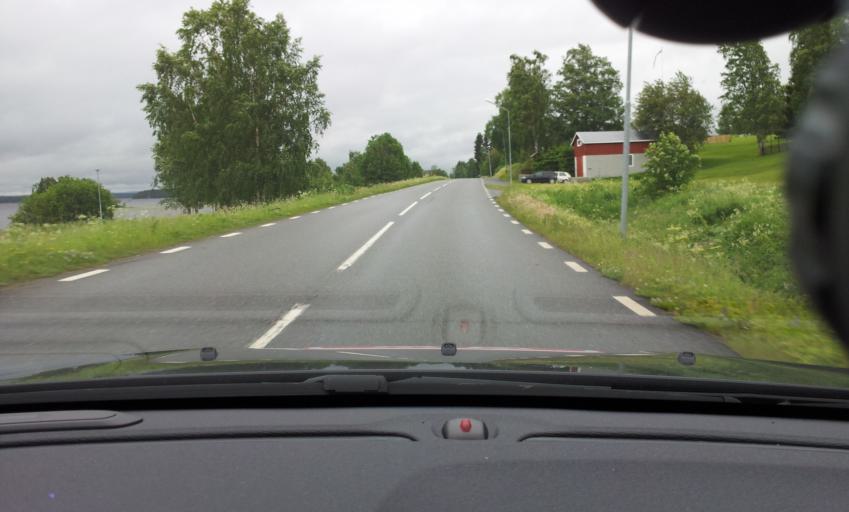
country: SE
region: Jaemtland
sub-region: Stroemsunds Kommun
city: Stroemsund
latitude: 63.5800
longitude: 15.3632
